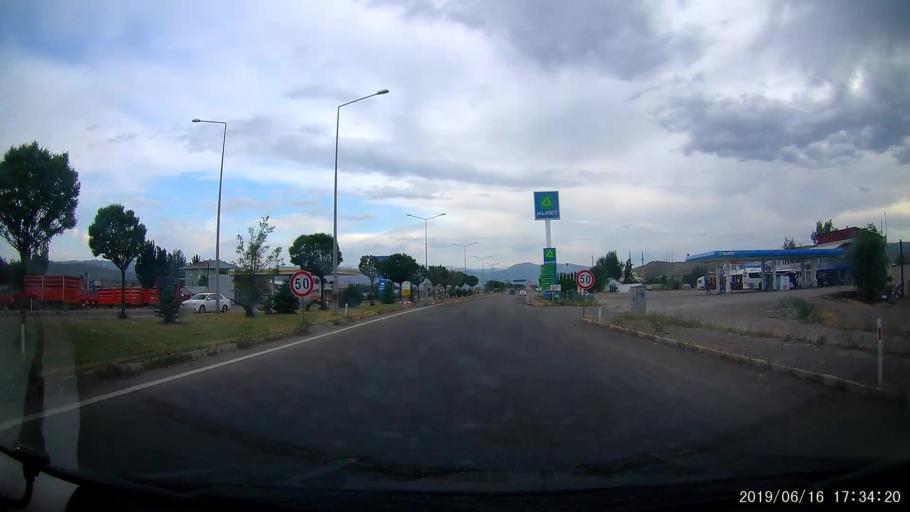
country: TR
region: Erzincan
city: Tercan
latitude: 39.7421
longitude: 40.2694
